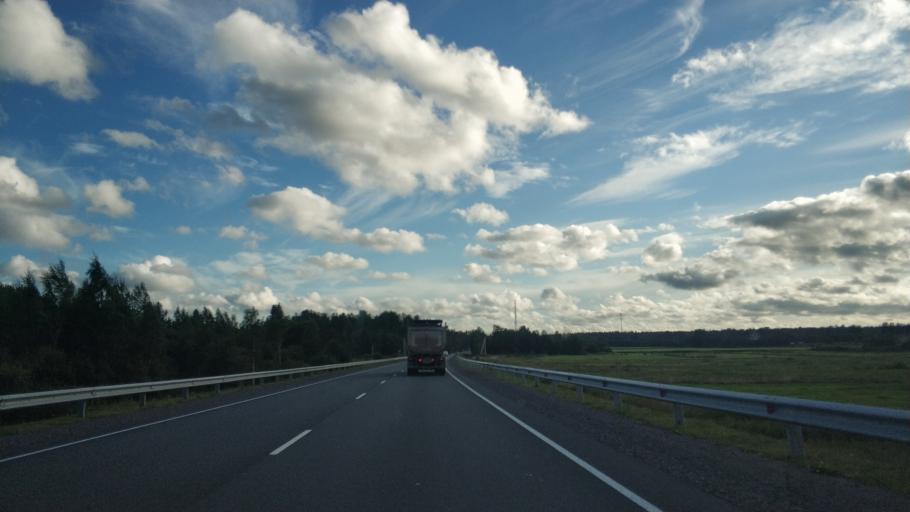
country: RU
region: Leningrad
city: Priozersk
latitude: 60.8614
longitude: 30.1577
